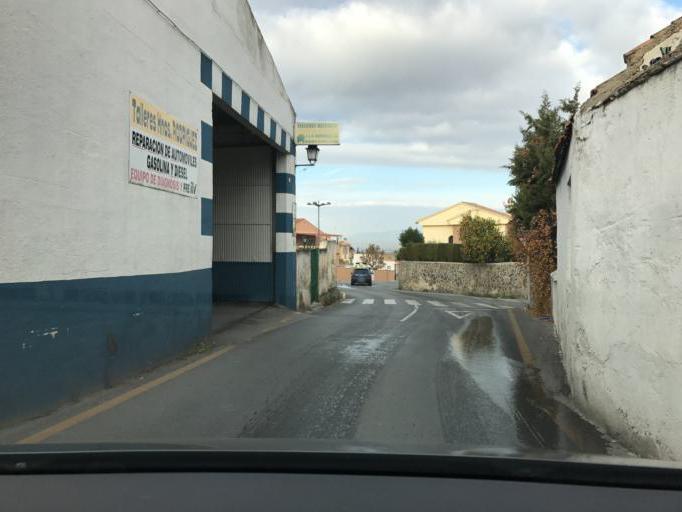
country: ES
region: Andalusia
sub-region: Provincia de Granada
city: Zubia
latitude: 37.1221
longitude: -3.5806
